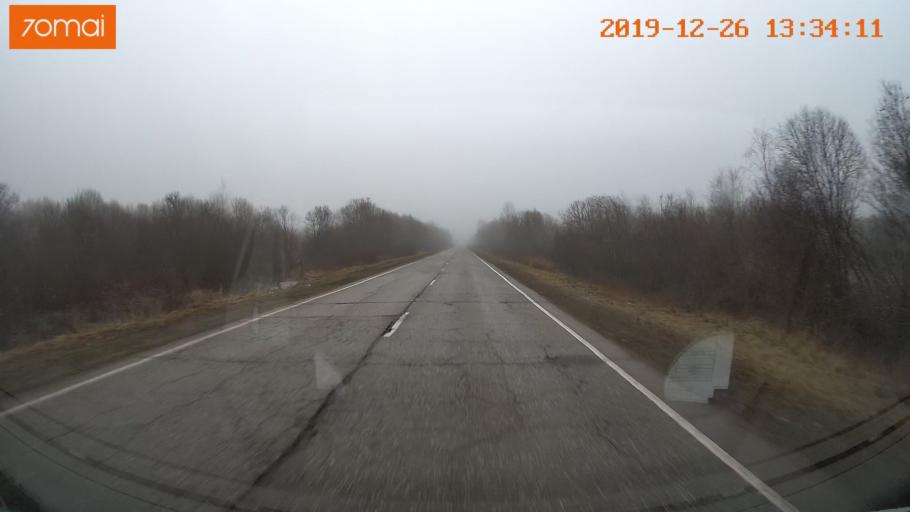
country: RU
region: Vologda
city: Sheksna
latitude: 58.8086
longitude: 38.3195
